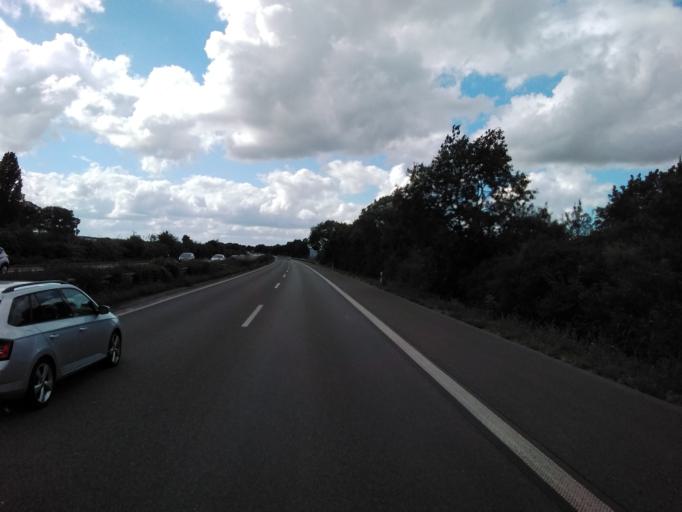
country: DE
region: North Rhine-Westphalia
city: Rheinberg
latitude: 51.5421
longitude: 6.5672
